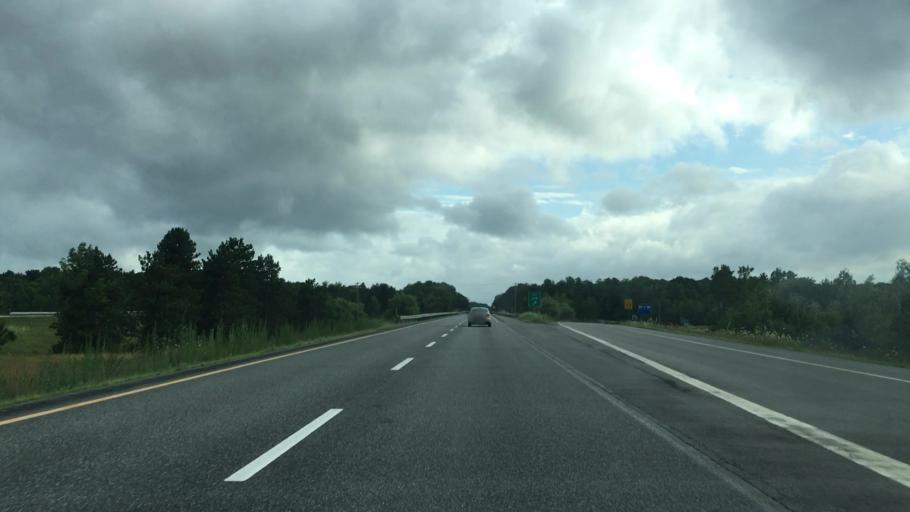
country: US
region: Maine
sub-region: Kennebec County
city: Clinton
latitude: 44.6422
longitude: -69.5261
